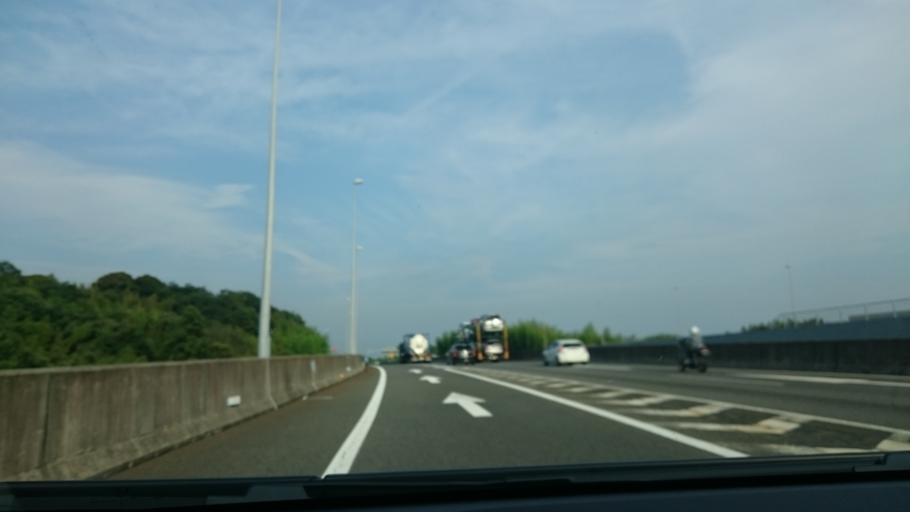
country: JP
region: Mie
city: Yokkaichi
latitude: 35.0374
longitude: 136.6316
